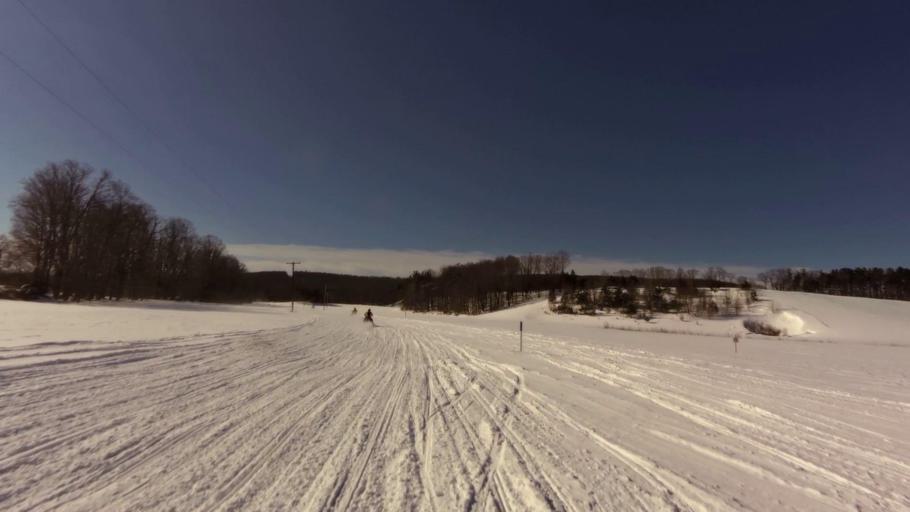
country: US
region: New York
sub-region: Cattaraugus County
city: Franklinville
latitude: 42.3669
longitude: -78.4651
